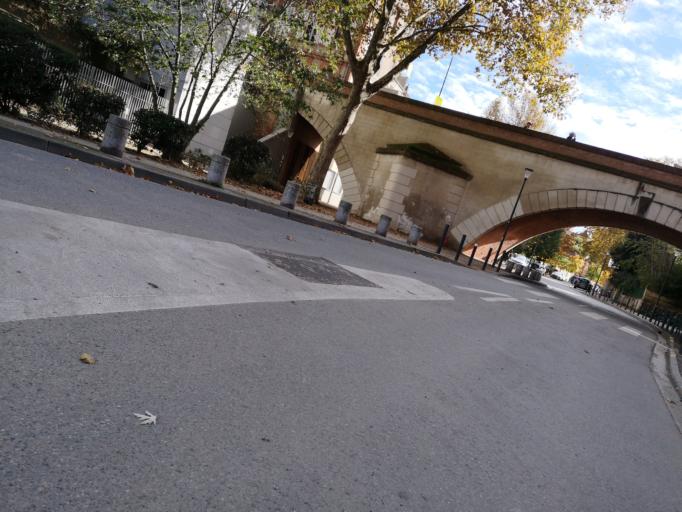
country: FR
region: Midi-Pyrenees
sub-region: Departement de la Haute-Garonne
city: Toulouse
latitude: 43.5979
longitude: 1.4410
